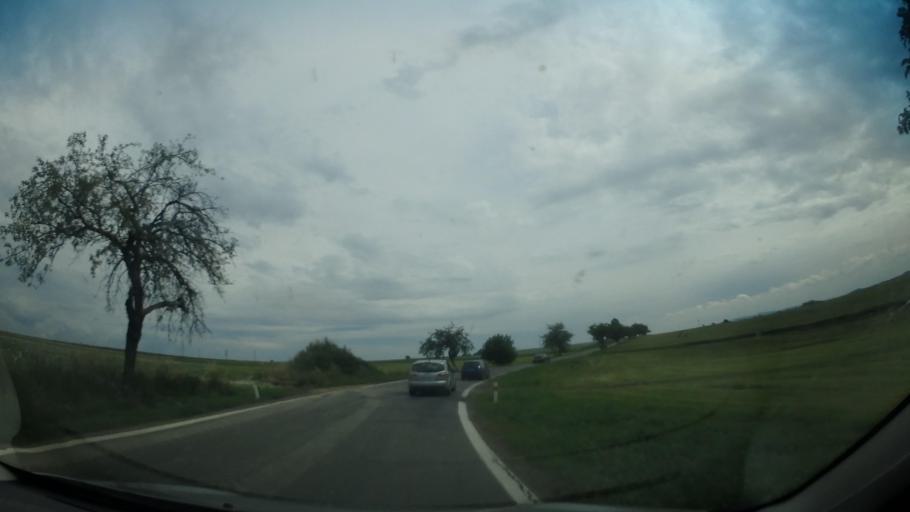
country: CZ
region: Vysocina
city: Bystrice nad Pernstejnem
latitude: 49.5014
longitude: 16.1731
